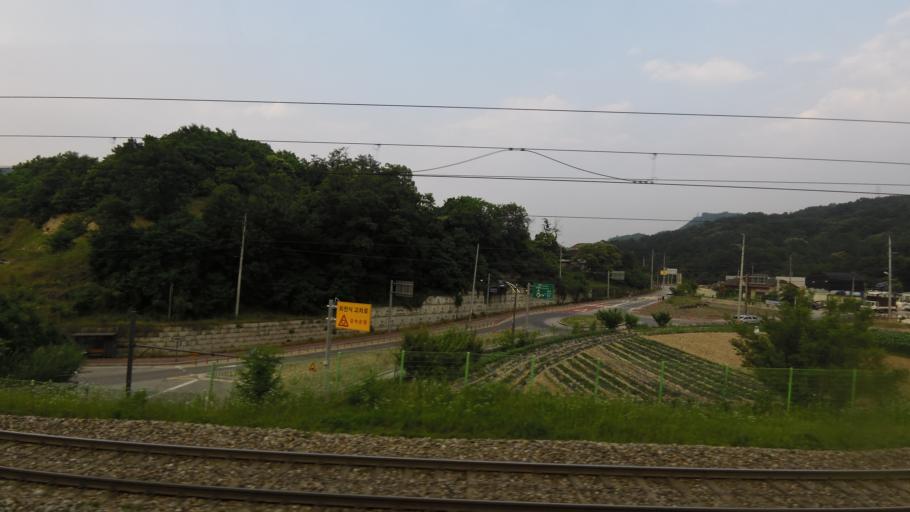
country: KR
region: Daejeon
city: Sintansin
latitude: 36.5272
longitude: 127.3734
